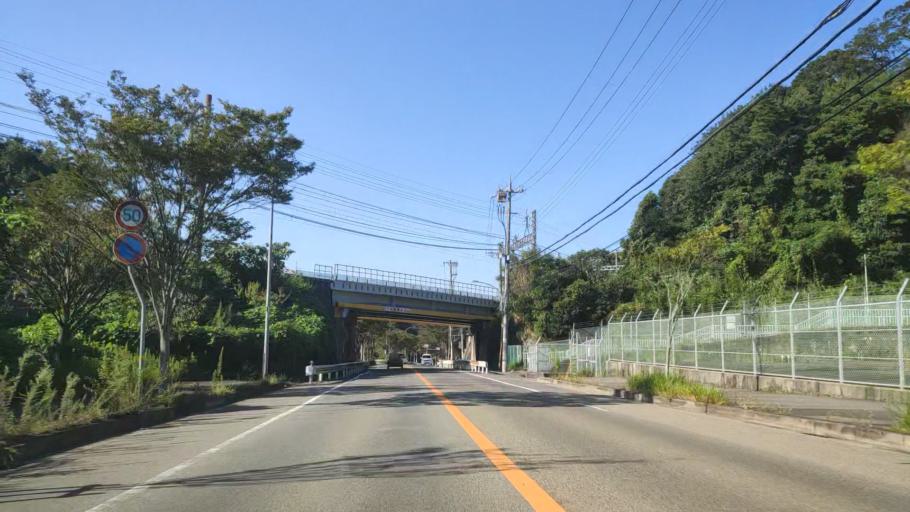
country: JP
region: Hyogo
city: Kobe
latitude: 34.7724
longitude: 135.1919
